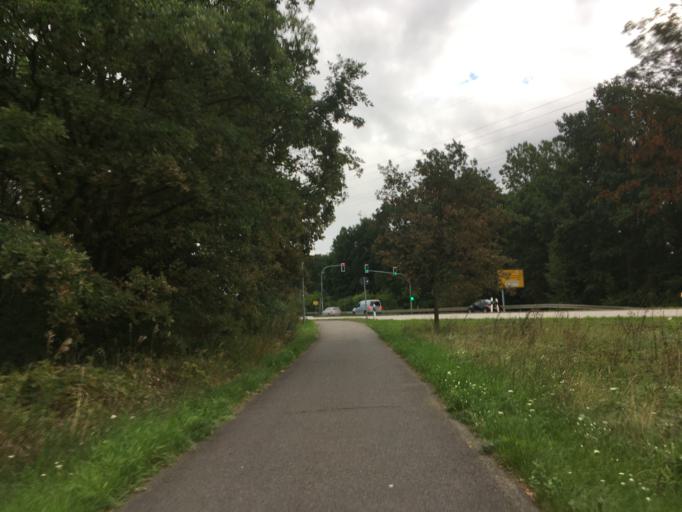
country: DE
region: Brandenburg
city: Meyenburg
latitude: 53.0774
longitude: 14.2436
